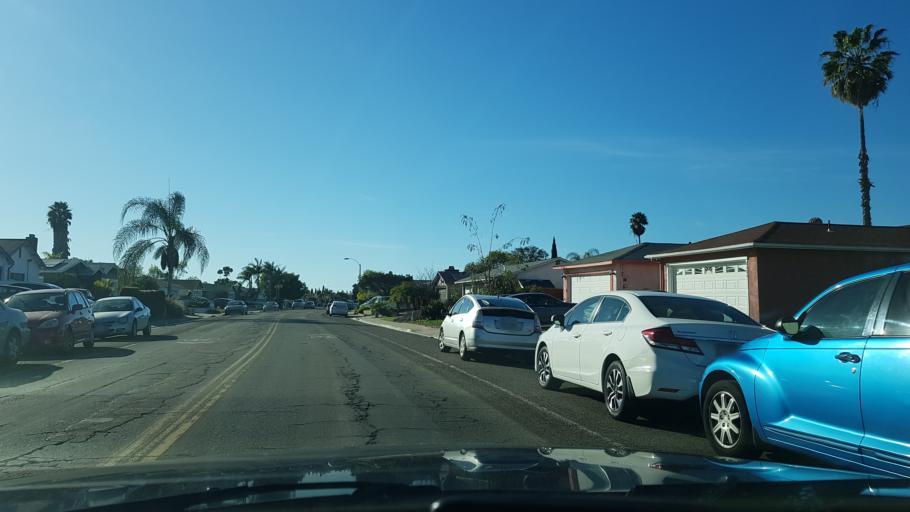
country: US
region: California
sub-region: San Diego County
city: Fairbanks Ranch
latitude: 32.9057
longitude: -117.1364
